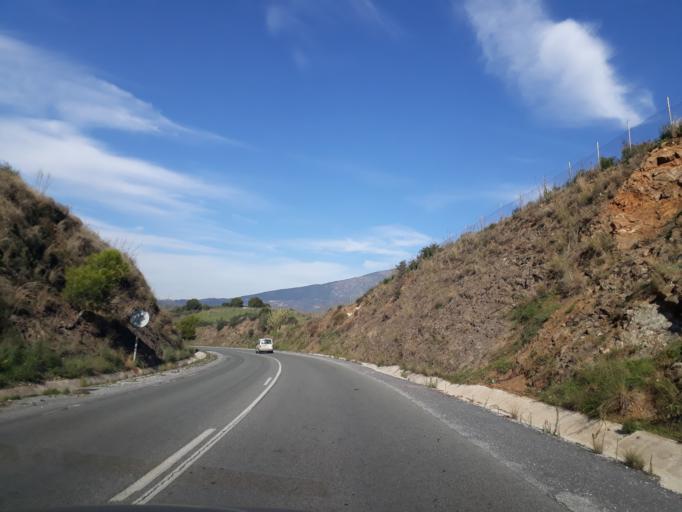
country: ES
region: Andalusia
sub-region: Provincia de Malaga
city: Fuengirola
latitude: 36.5354
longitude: -4.6859
